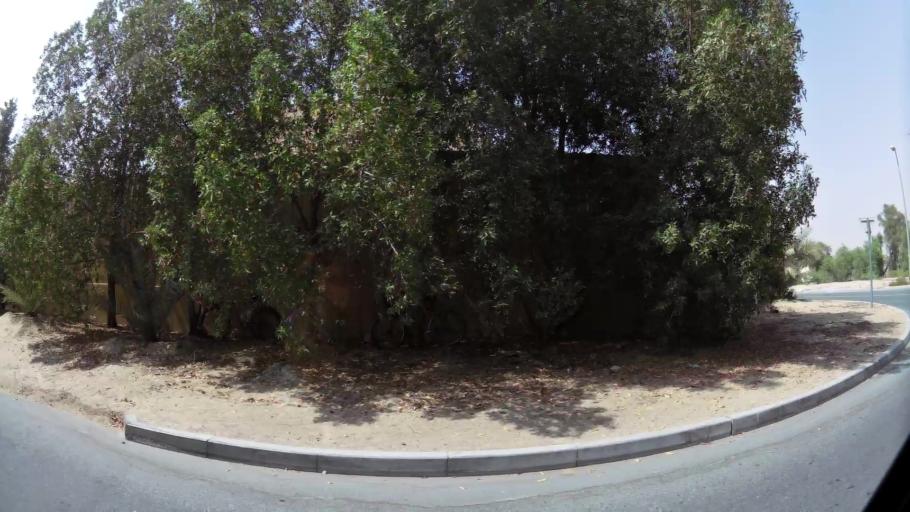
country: AE
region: Ash Shariqah
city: Sharjah
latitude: 25.2332
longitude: 55.4426
